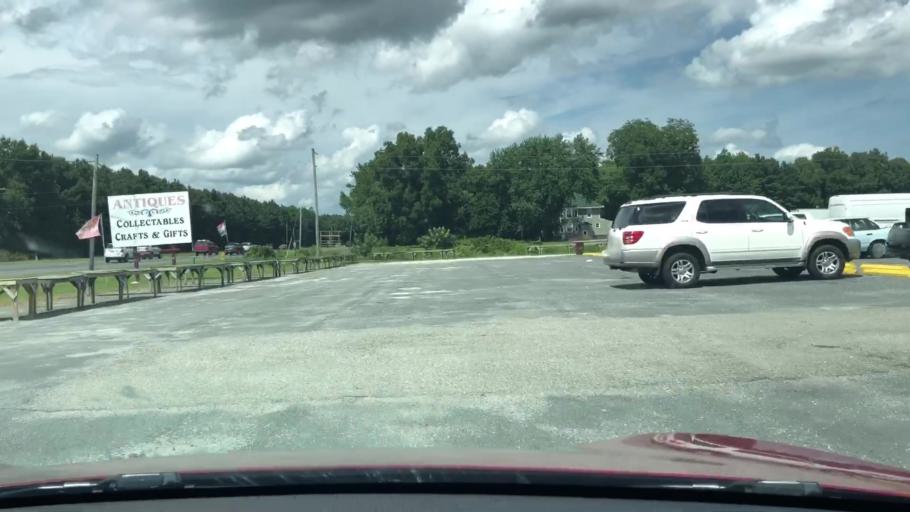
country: US
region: Virginia
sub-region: Accomack County
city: Wattsville
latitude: 37.8738
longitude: -75.5581
